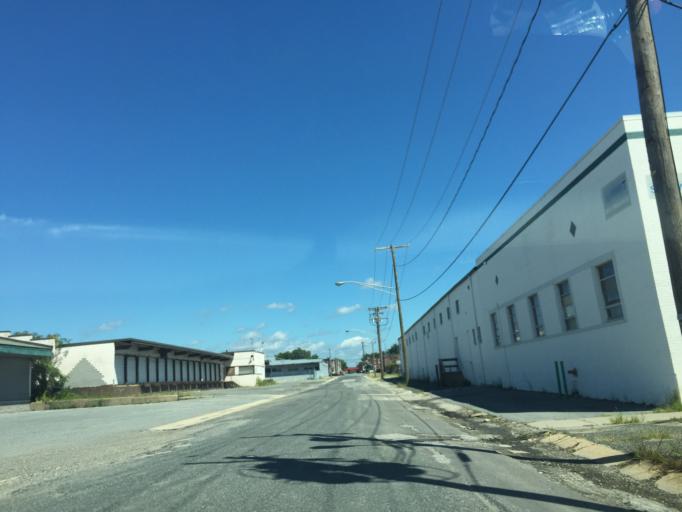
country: US
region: Maryland
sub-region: City of Baltimore
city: Baltimore
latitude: 39.2890
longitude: -76.5597
